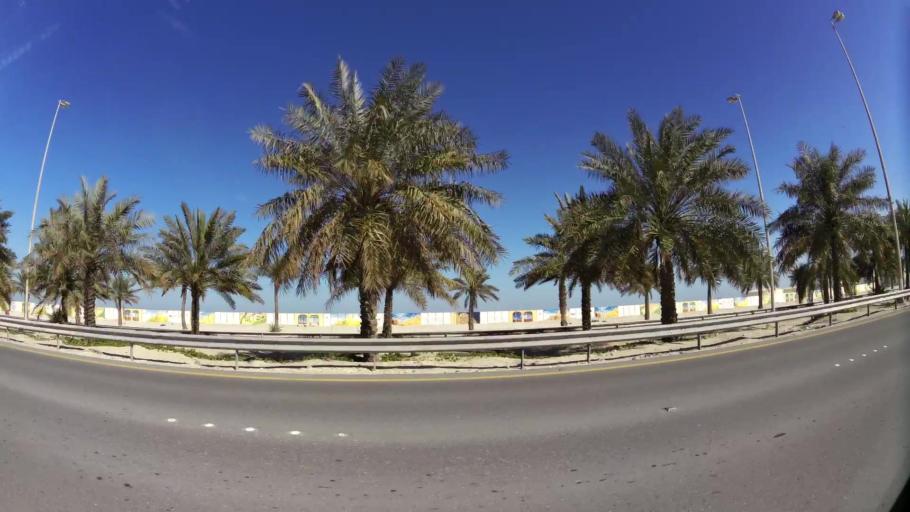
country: BH
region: Muharraq
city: Al Hadd
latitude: 26.2369
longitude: 50.6576
